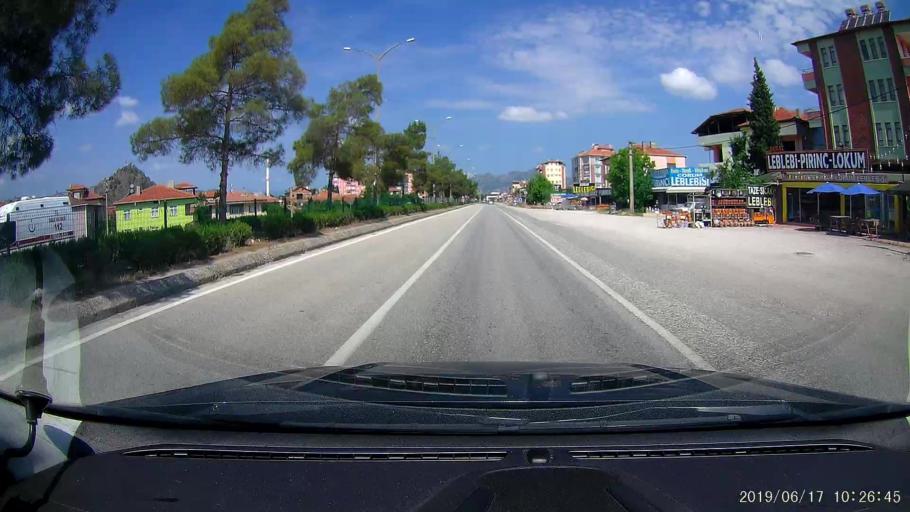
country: TR
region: Corum
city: Osmancik
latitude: 40.9751
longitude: 34.8153
